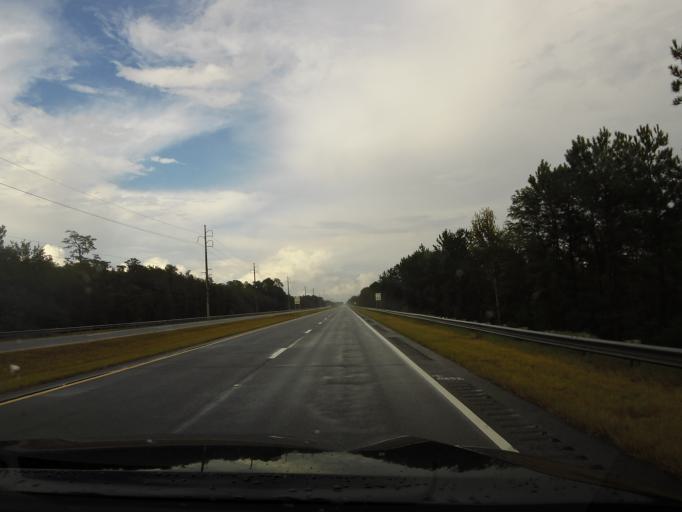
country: US
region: Georgia
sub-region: Long County
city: Ludowici
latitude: 31.6917
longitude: -81.7859
